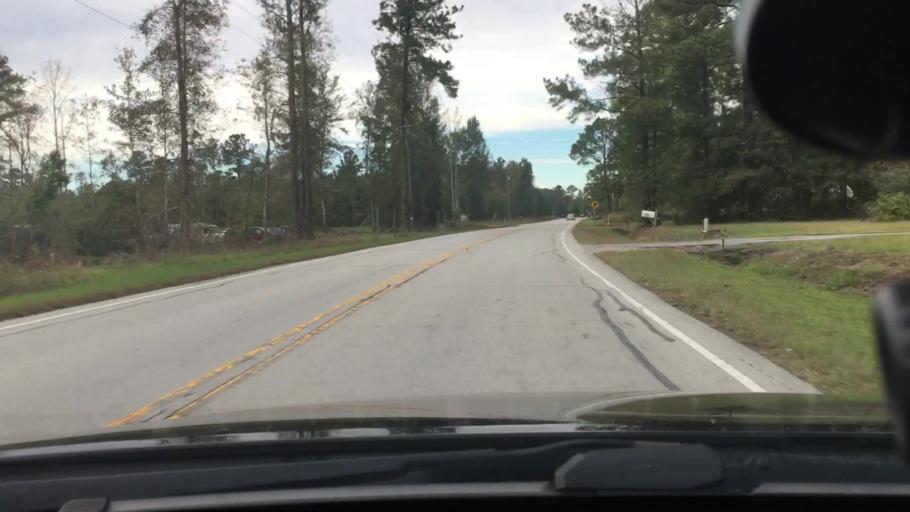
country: US
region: North Carolina
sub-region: Craven County
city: Vanceboro
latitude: 35.3293
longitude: -77.1707
